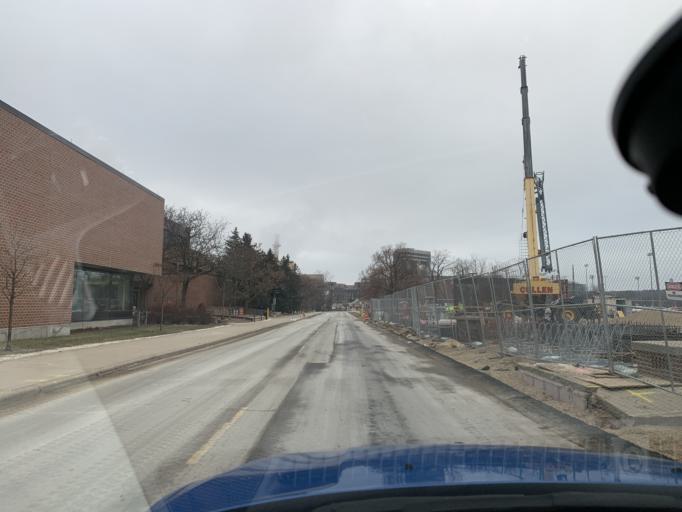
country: US
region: Wisconsin
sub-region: Dane County
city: Madison
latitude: 43.0756
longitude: -89.4193
